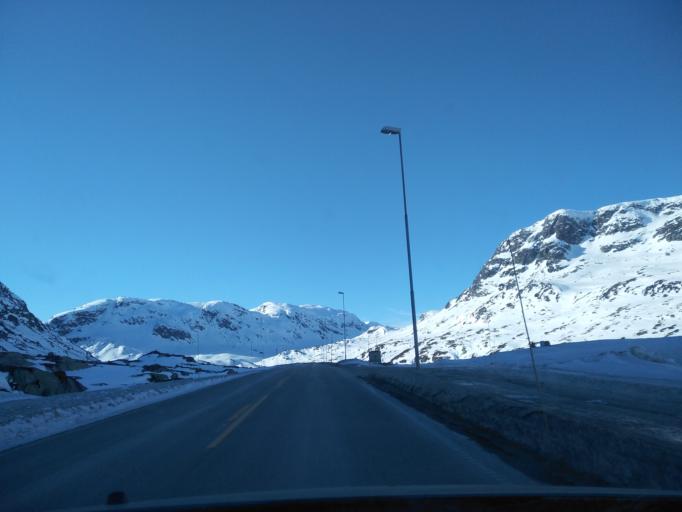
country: NO
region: Aust-Agder
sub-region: Bykle
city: Hovden
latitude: 59.8505
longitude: 7.1074
